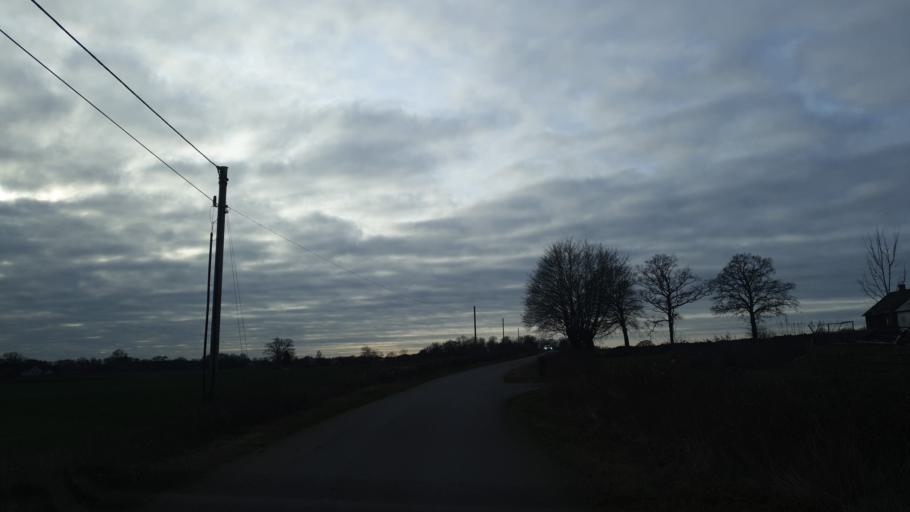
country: SE
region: Kalmar
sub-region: Torsas Kommun
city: Torsas
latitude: 56.3303
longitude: 16.0456
